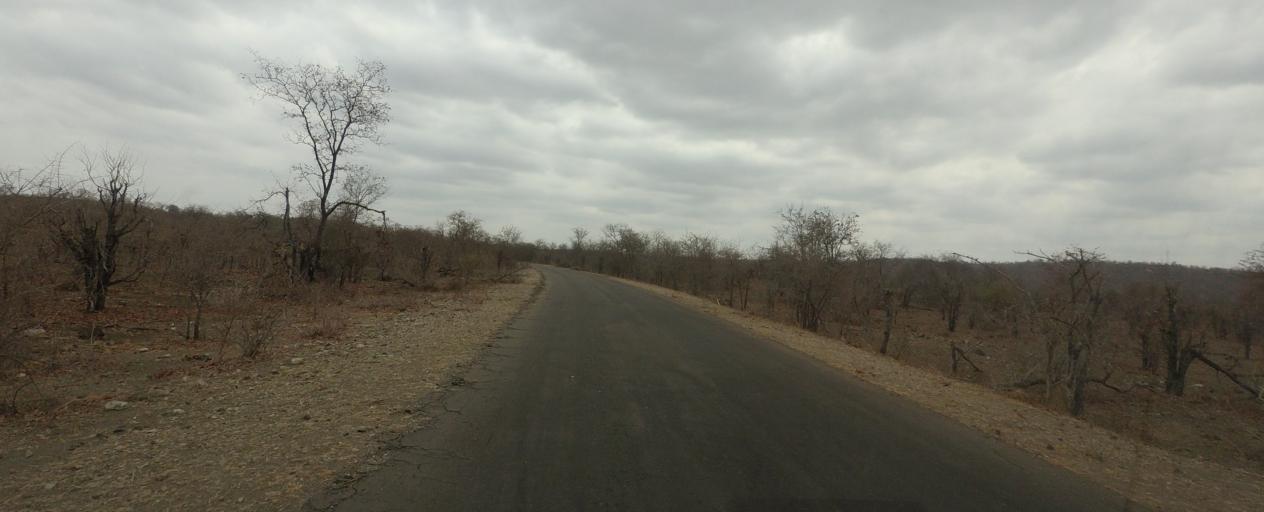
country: ZA
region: Limpopo
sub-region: Vhembe District Municipality
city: Mutale
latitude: -22.4041
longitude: 31.2083
